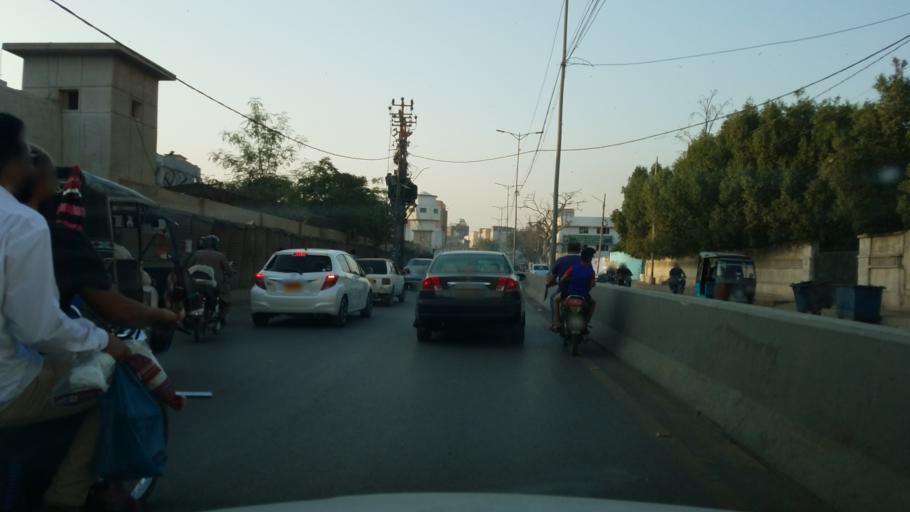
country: PK
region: Sindh
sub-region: Karachi District
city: Karachi
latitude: 24.8696
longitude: 67.0226
